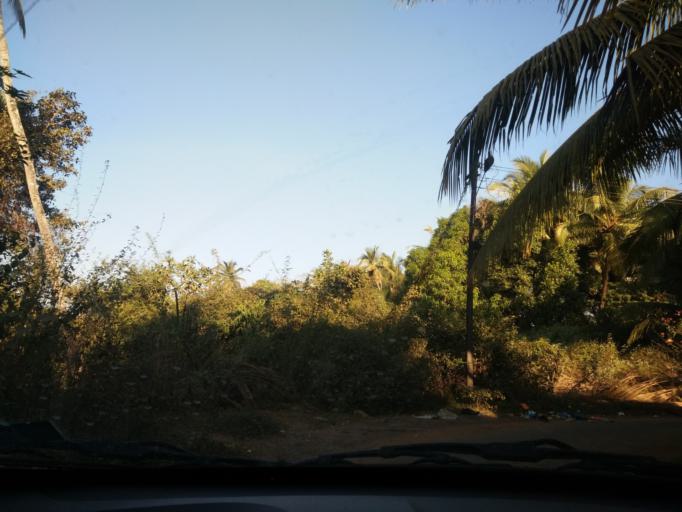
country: IN
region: Goa
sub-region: South Goa
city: Madgaon
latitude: 15.2554
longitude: 73.9545
